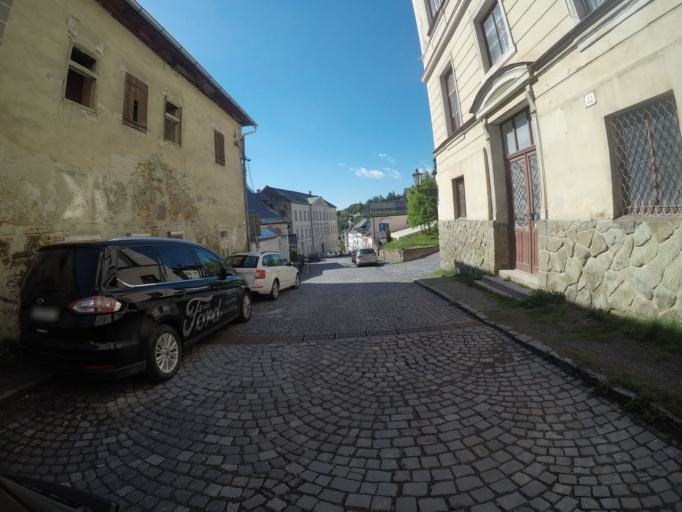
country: SK
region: Banskobystricky
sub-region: Okres Banska Bystrica
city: Banska Stiavnica
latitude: 48.4614
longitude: 18.8917
